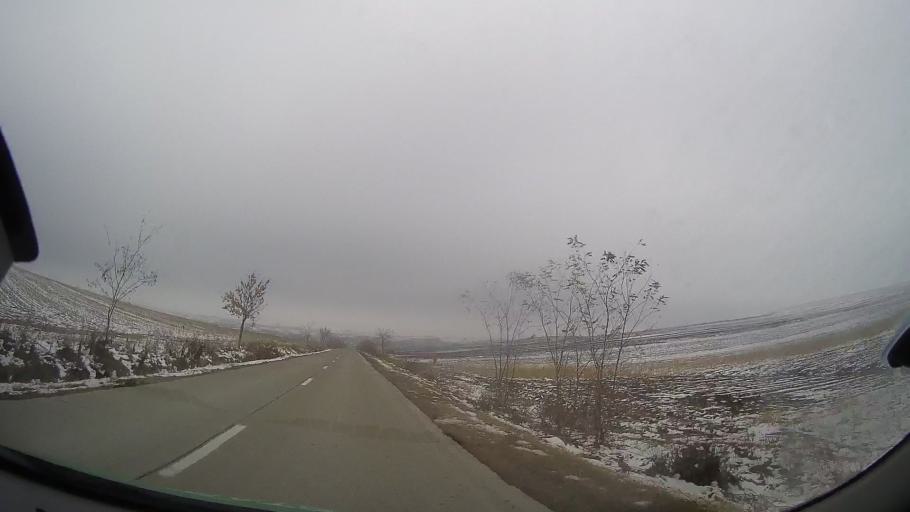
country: RO
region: Vaslui
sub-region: Comuna Ivesti
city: Ivesti
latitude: 46.1983
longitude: 27.5148
